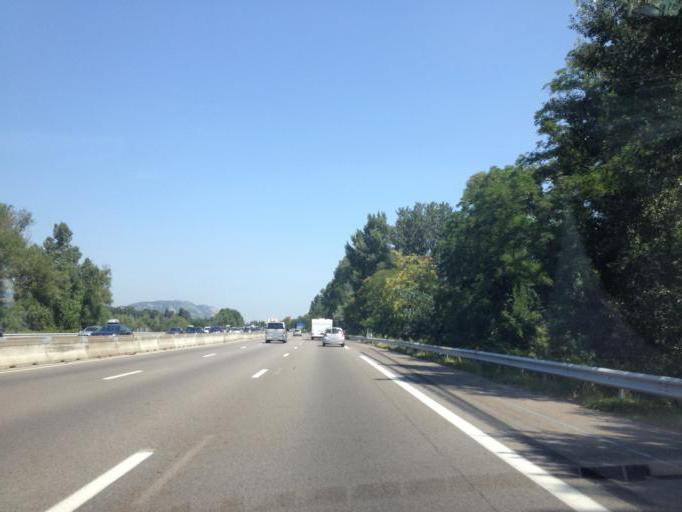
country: FR
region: Rhone-Alpes
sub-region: Departement de la Drome
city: Portes-les-Valence
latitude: 44.8572
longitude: 4.8670
